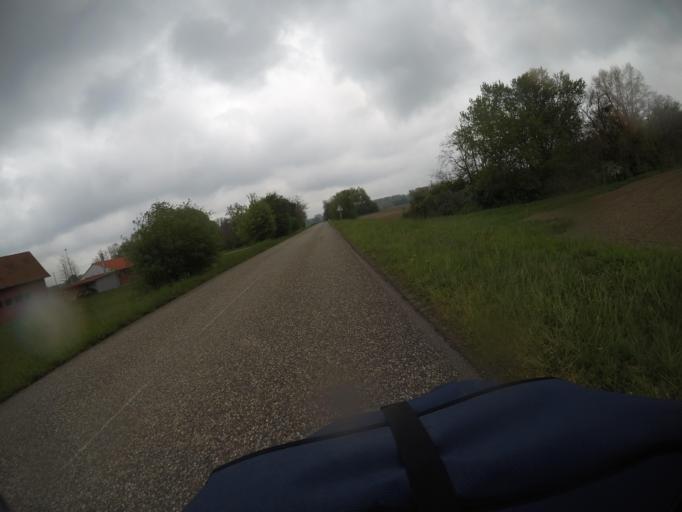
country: FR
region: Alsace
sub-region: Departement du Bas-Rhin
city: Roppenheim
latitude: 48.8221
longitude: 8.0735
